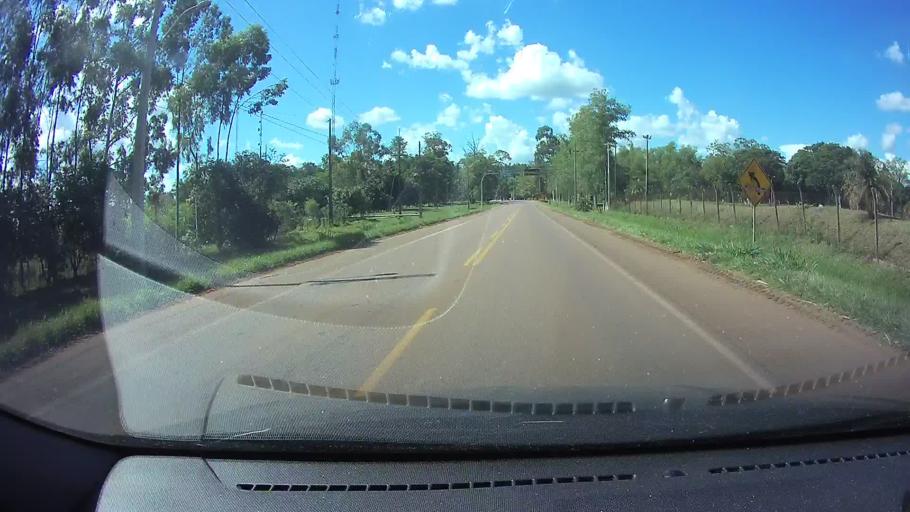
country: PY
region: Guaira
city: Coronel Martinez
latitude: -25.7729
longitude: -56.6520
